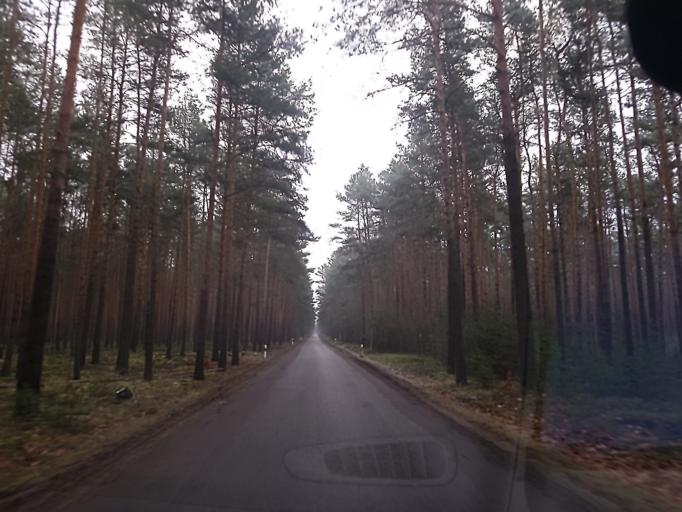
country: DE
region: Brandenburg
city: Crinitz
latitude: 51.7022
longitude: 13.7581
